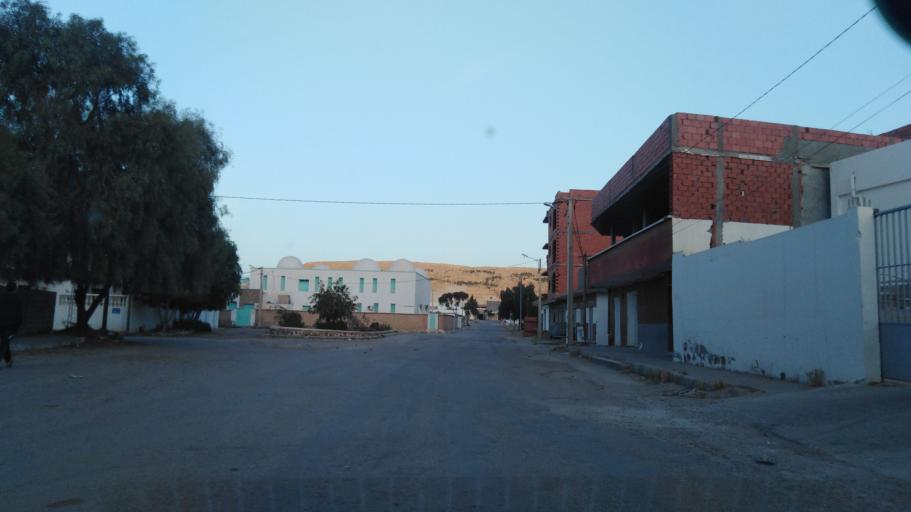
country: TN
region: Tataouine
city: Tataouine
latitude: 32.9409
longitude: 10.4529
